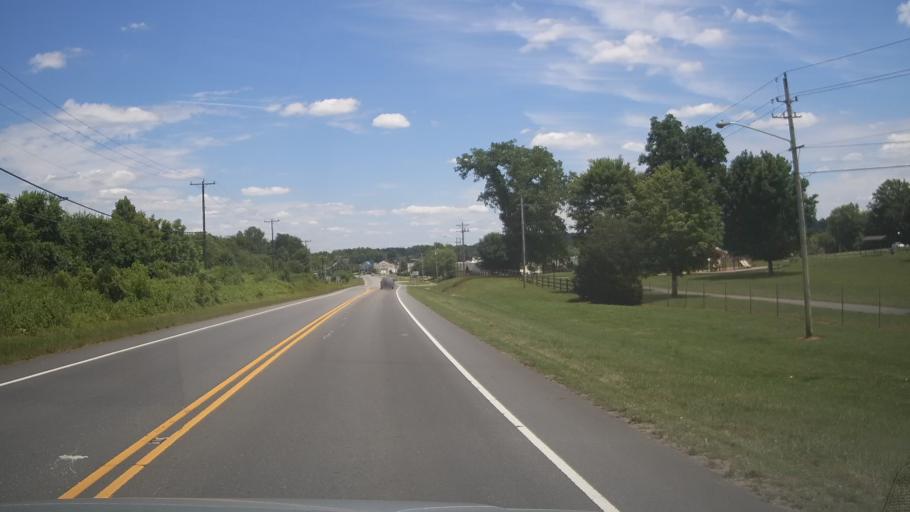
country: US
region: North Carolina
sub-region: Burke County
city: Morganton
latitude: 35.7488
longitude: -81.7189
